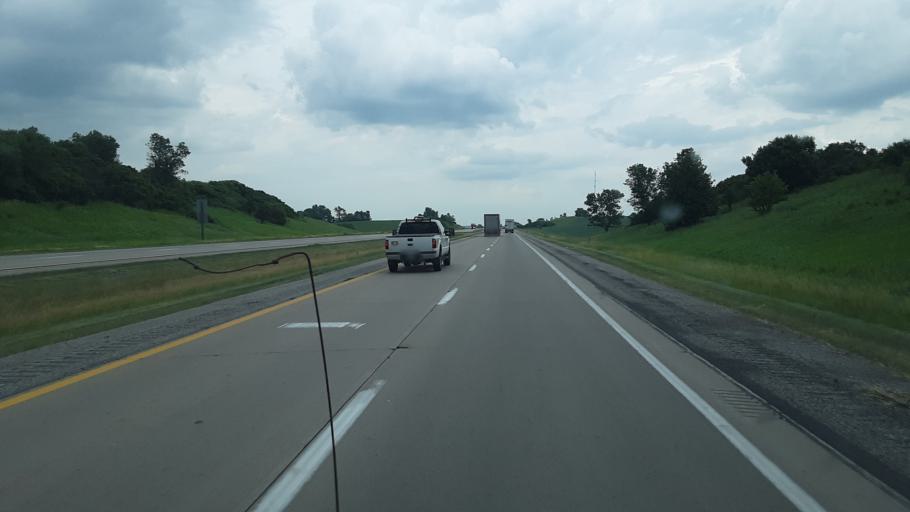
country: US
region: Iowa
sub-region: Pottawattamie County
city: Avoca
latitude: 41.4838
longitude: -95.5877
